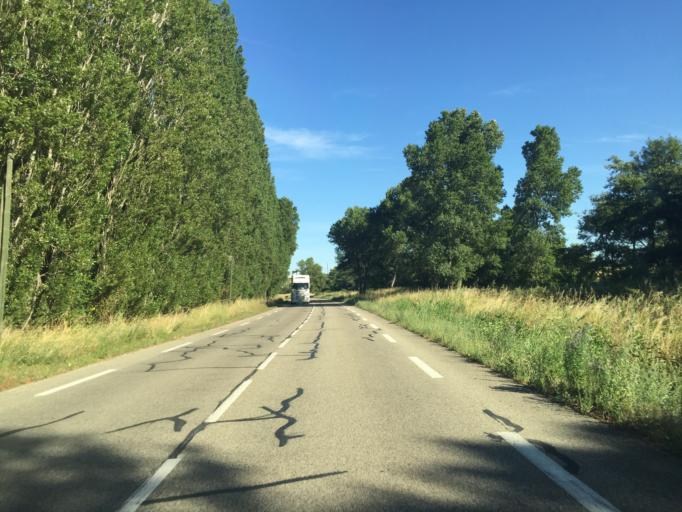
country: FR
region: Languedoc-Roussillon
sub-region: Departement du Gard
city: Montfaucon
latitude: 44.0784
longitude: 4.7631
